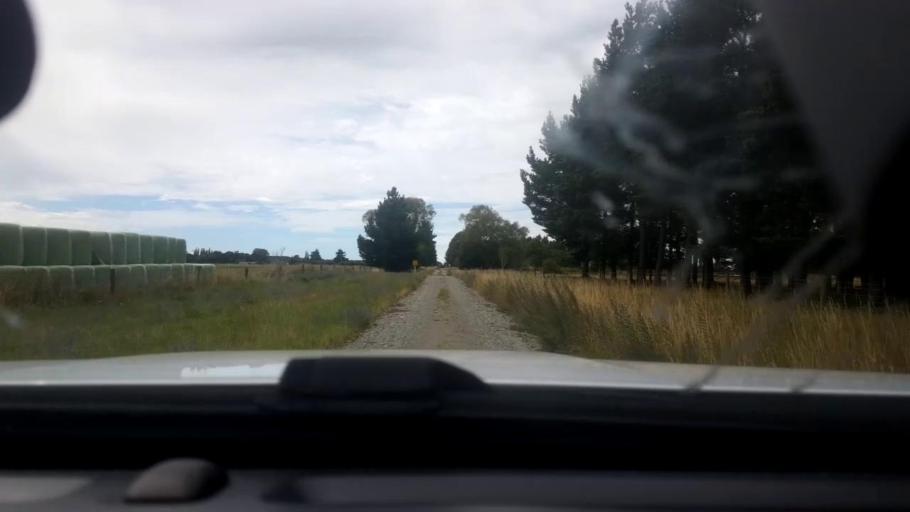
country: NZ
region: Canterbury
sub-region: Timaru District
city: Pleasant Point
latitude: -44.1329
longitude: 171.2830
